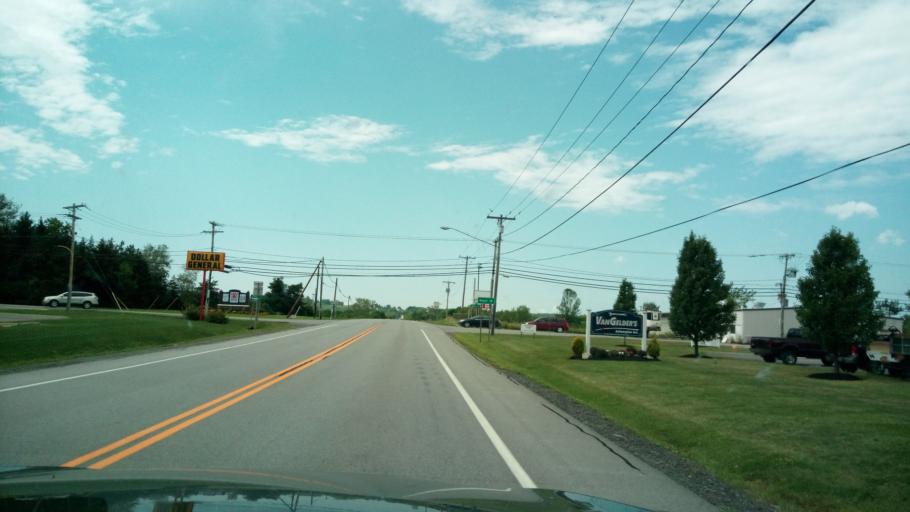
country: US
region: New York
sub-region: Livingston County
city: Geneseo
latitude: 42.8306
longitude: -77.8812
